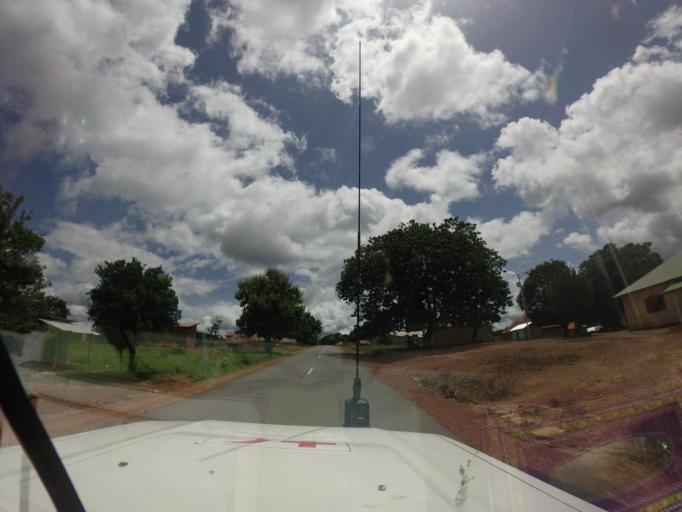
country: SL
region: Northern Province
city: Bindi
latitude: 10.1711
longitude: -11.4059
